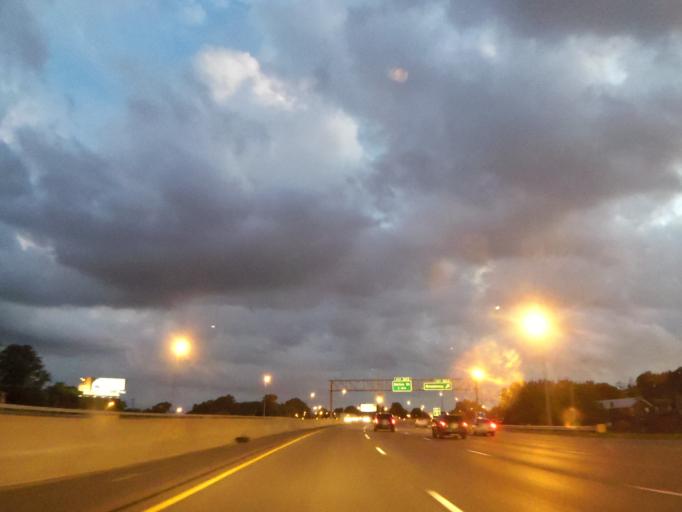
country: US
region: Illinois
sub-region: Saint Clair County
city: Cahokia
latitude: 38.5761
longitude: -90.2305
